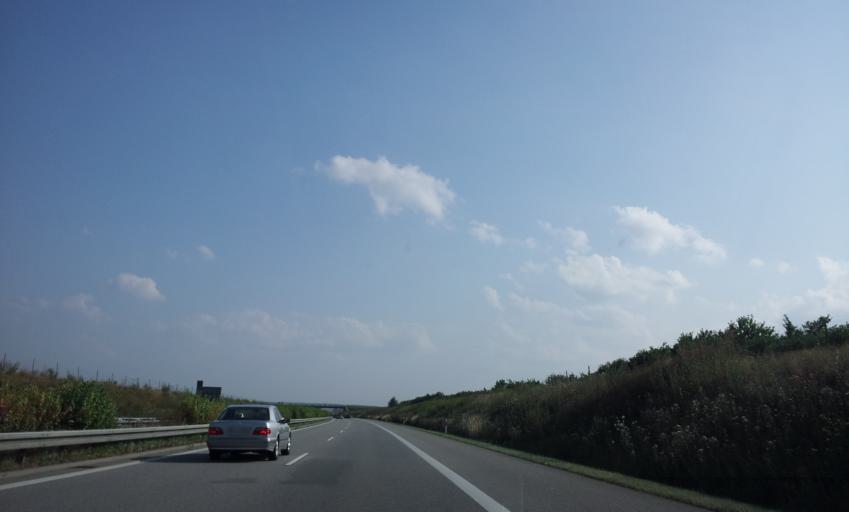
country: DE
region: Mecklenburg-Vorpommern
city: Kessin
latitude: 53.7014
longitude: 13.3260
